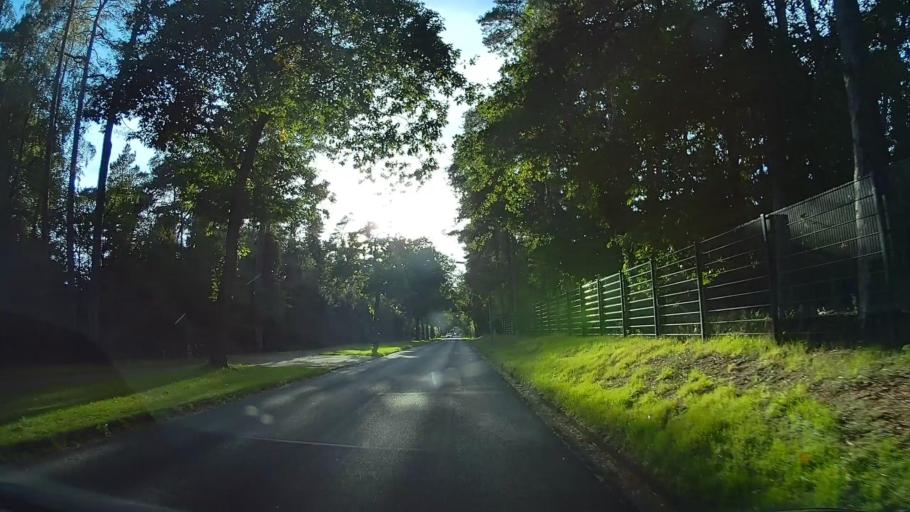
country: DE
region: Lower Saxony
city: Hellwege
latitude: 53.0733
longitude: 9.2239
